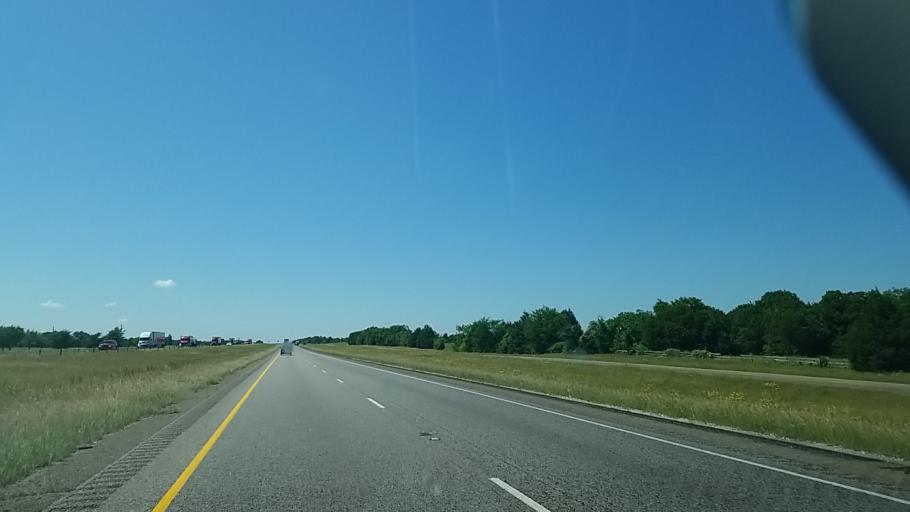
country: US
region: Texas
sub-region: Freestone County
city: Fairfield
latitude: 31.7661
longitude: -96.2153
